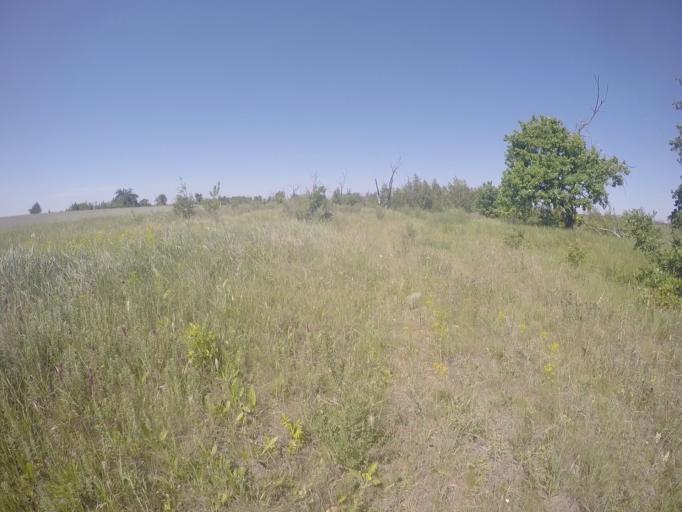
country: RU
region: Saratov
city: Krasnyy Oktyabr'
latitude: 51.2950
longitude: 45.5546
